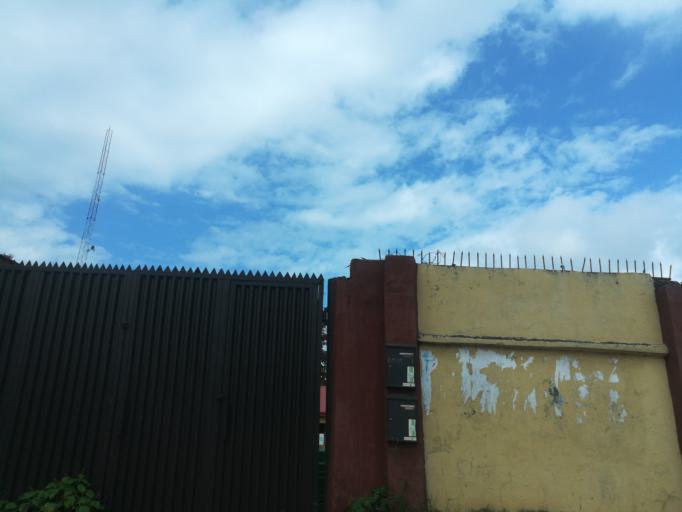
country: NG
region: Lagos
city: Agege
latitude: 6.6243
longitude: 3.3309
